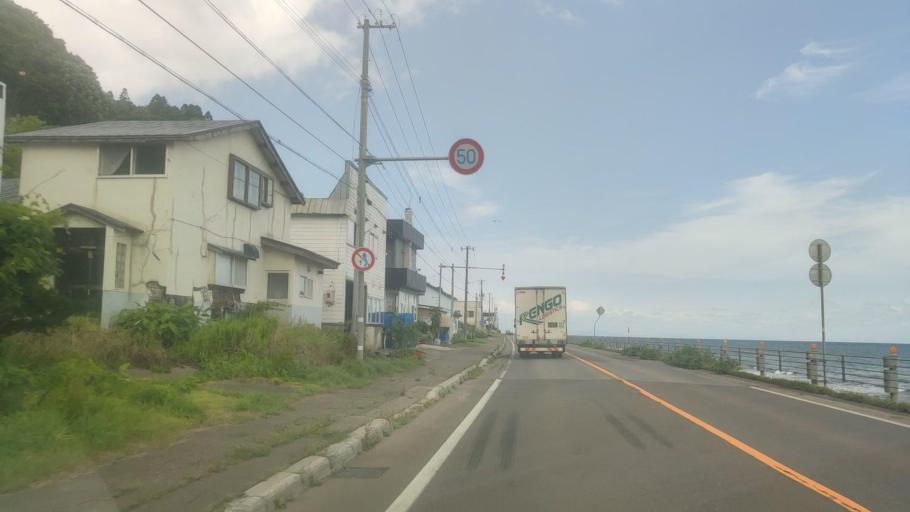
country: JP
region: Hokkaido
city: Nanae
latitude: 42.1425
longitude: 140.5020
